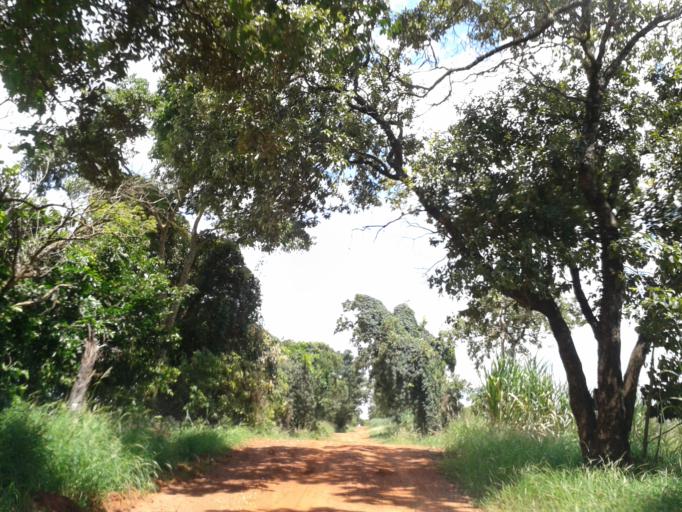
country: BR
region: Minas Gerais
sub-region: Ituiutaba
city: Ituiutaba
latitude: -18.8590
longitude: -49.4976
